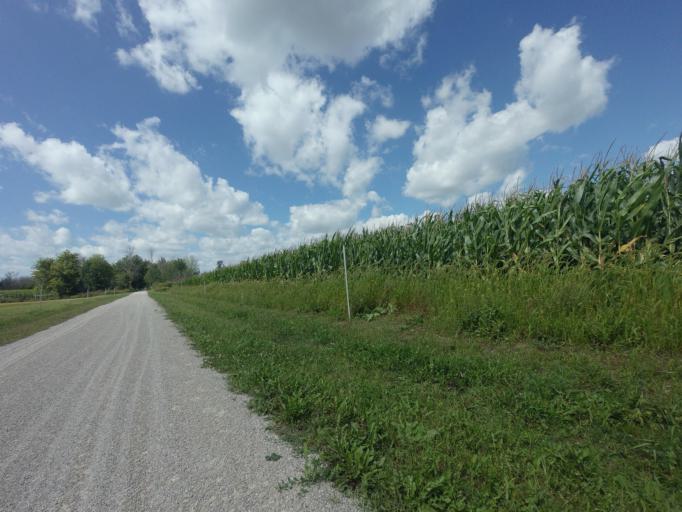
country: CA
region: Ontario
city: Huron East
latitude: 43.6110
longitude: -81.1318
